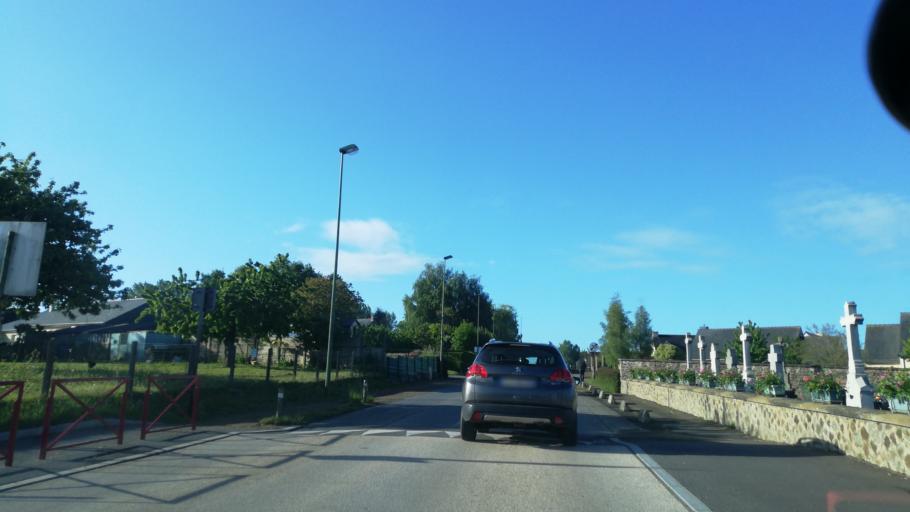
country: FR
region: Brittany
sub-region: Departement d'Ille-et-Vilaine
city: Irodouer
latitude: 48.2463
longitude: -1.9494
